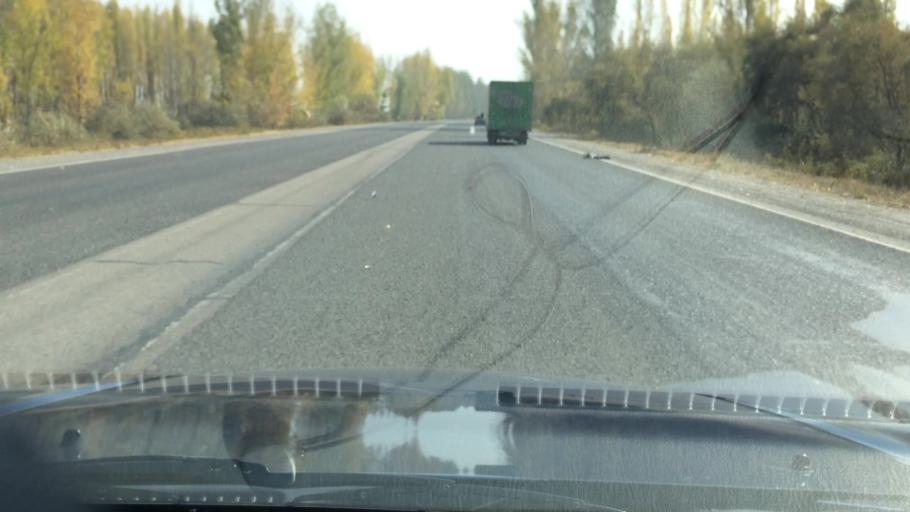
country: KG
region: Chuy
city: Ivanovka
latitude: 42.9372
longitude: 74.9874
